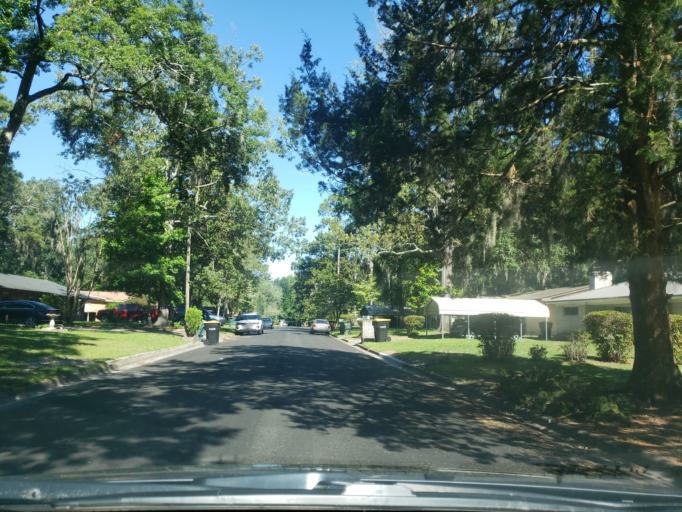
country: US
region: Georgia
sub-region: Chatham County
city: Montgomery
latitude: 31.9880
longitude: -81.1395
